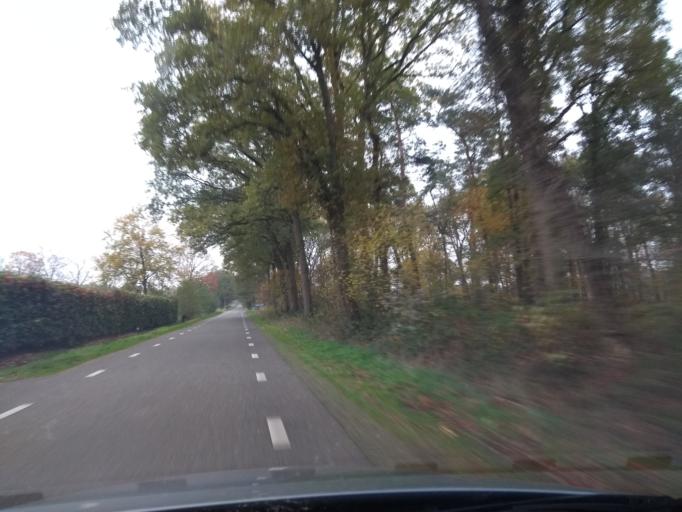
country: NL
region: Gelderland
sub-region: Gemeente Bronckhorst
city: Hengelo
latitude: 52.0374
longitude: 6.3382
